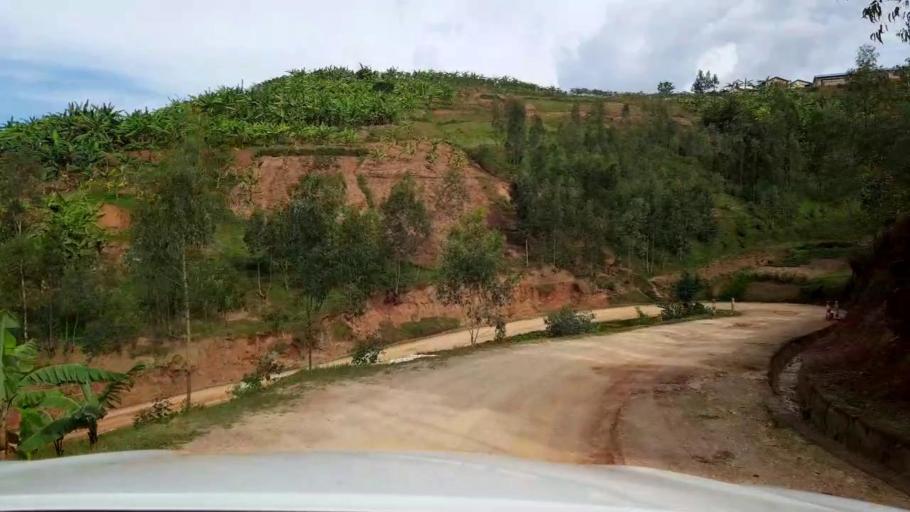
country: RW
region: Southern Province
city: Gitarama
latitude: -1.9753
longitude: 29.7096
